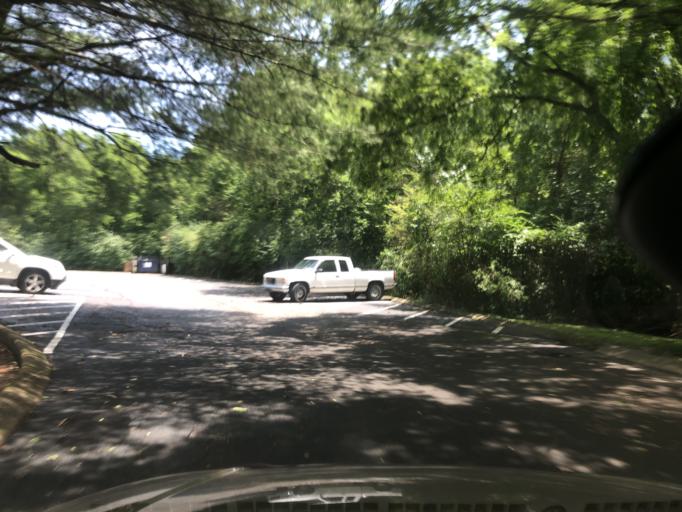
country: US
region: Tennessee
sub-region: Davidson County
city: Lakewood
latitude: 36.2487
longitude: -86.7021
